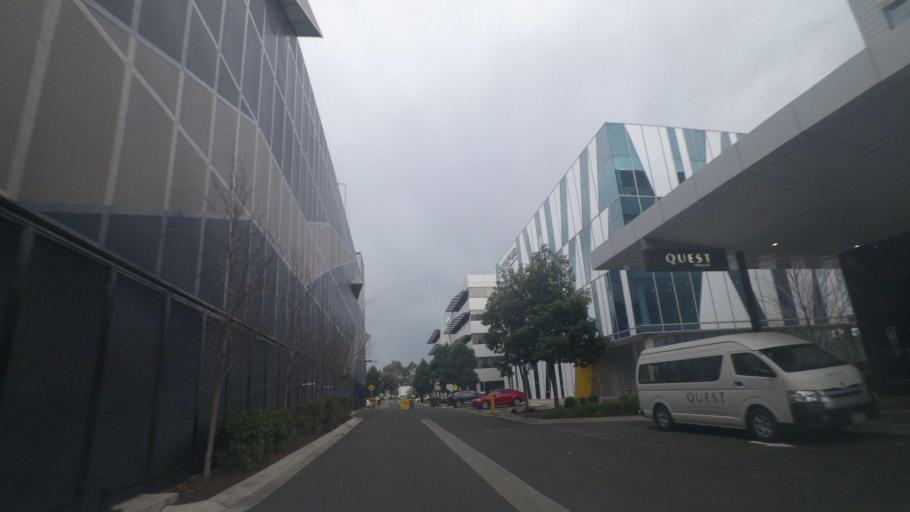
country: AU
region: Victoria
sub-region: Monash
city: Notting Hill
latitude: -37.9019
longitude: 145.1342
